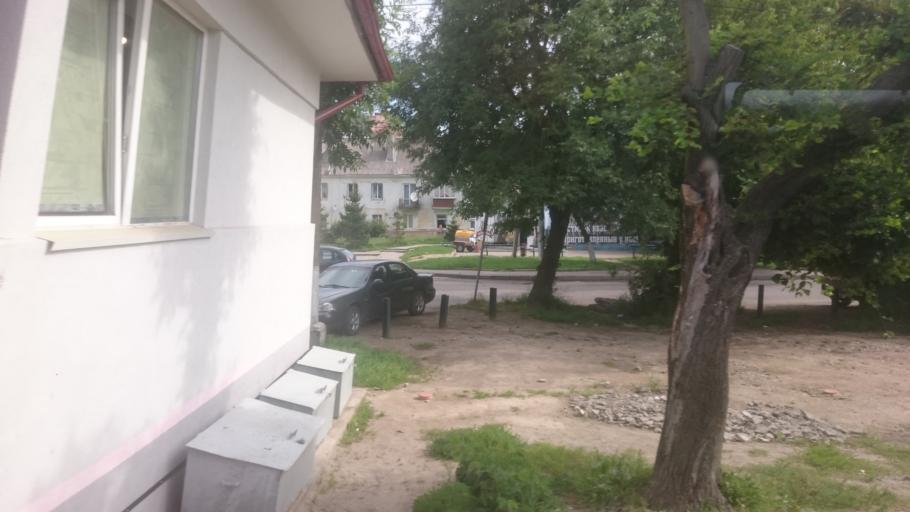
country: RU
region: Kaliningrad
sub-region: Gorod Kaliningrad
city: Pionerskiy
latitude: 54.9487
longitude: 20.2257
